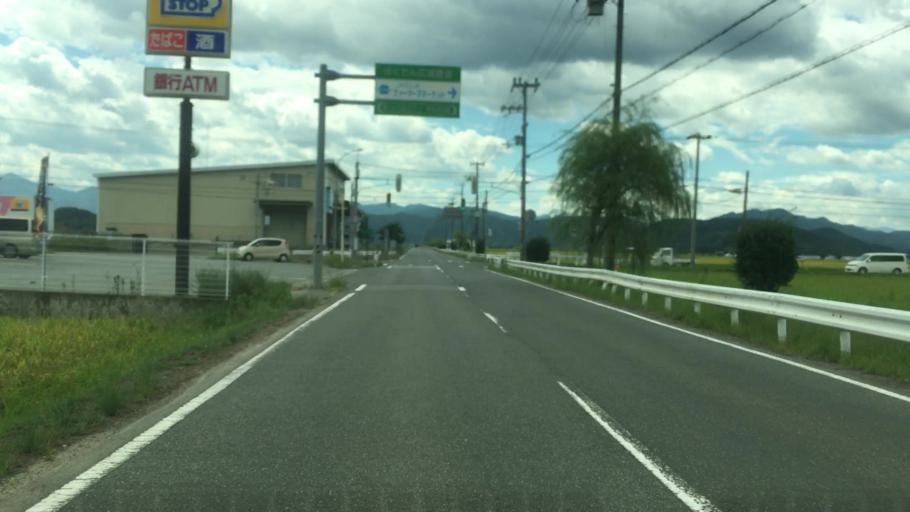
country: JP
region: Hyogo
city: Toyooka
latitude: 35.5253
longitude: 134.8398
